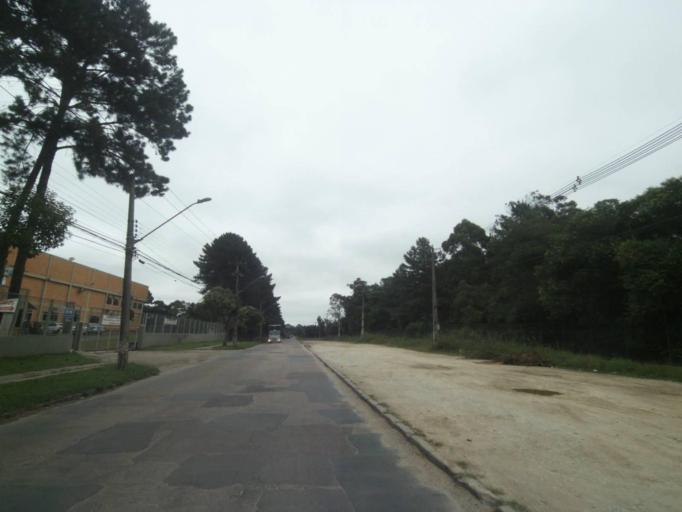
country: BR
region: Parana
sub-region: Araucaria
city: Araucaria
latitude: -25.5376
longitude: -49.3189
